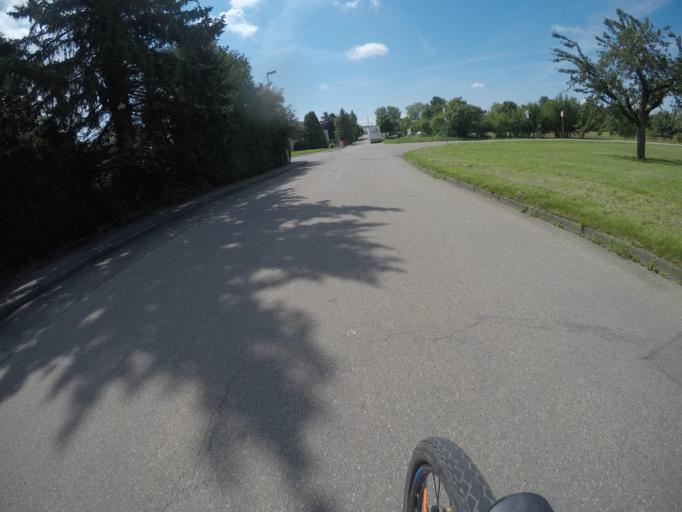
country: DE
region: Baden-Wuerttemberg
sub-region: Regierungsbezirk Stuttgart
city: Deckenpfronn
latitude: 48.6237
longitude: 8.8284
